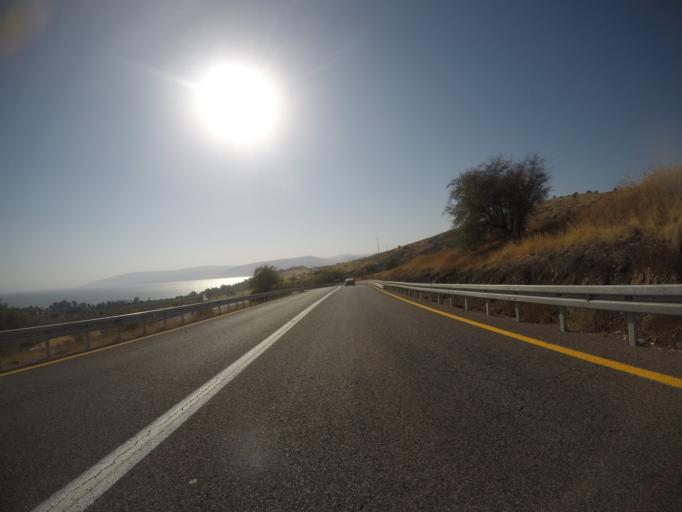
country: IL
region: Northern District
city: Rosh Pinna
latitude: 32.8802
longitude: 35.5475
